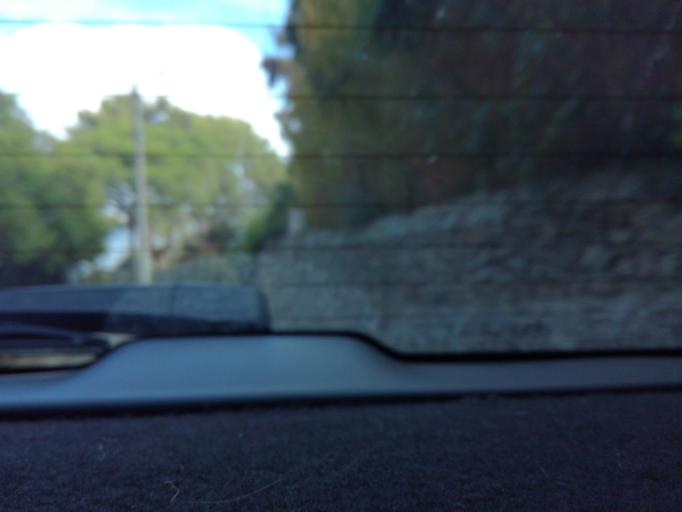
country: FR
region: Provence-Alpes-Cote d'Azur
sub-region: Departement du Var
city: Carqueiranne
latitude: 43.0370
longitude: 6.1299
